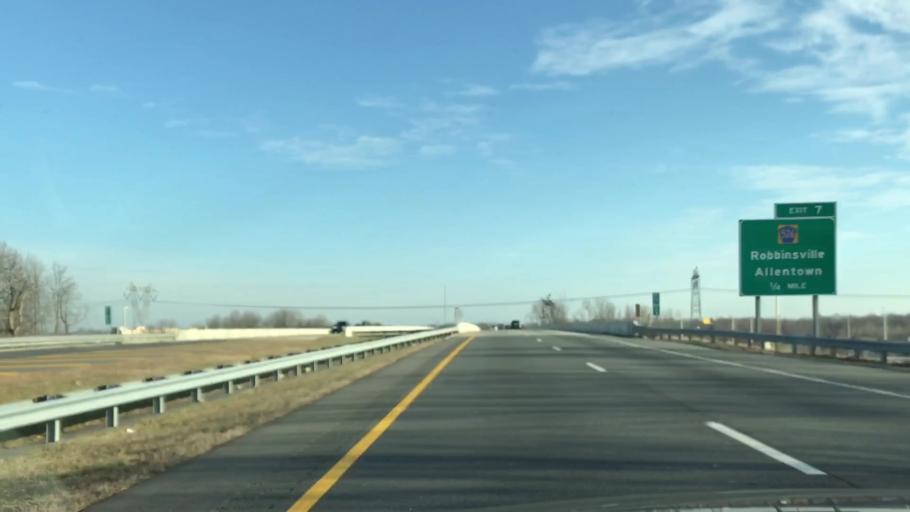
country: US
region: New Jersey
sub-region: Monmouth County
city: Allentown
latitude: 40.1941
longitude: -74.6024
